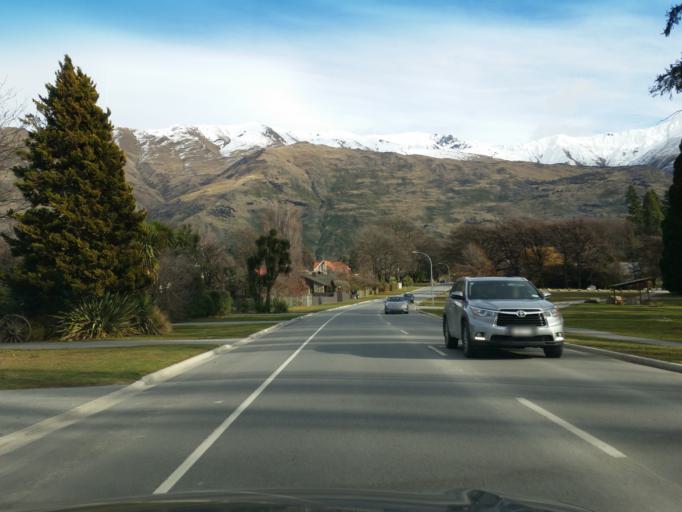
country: NZ
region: Otago
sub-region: Queenstown-Lakes District
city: Wanaka
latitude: -44.7000
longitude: 169.1223
